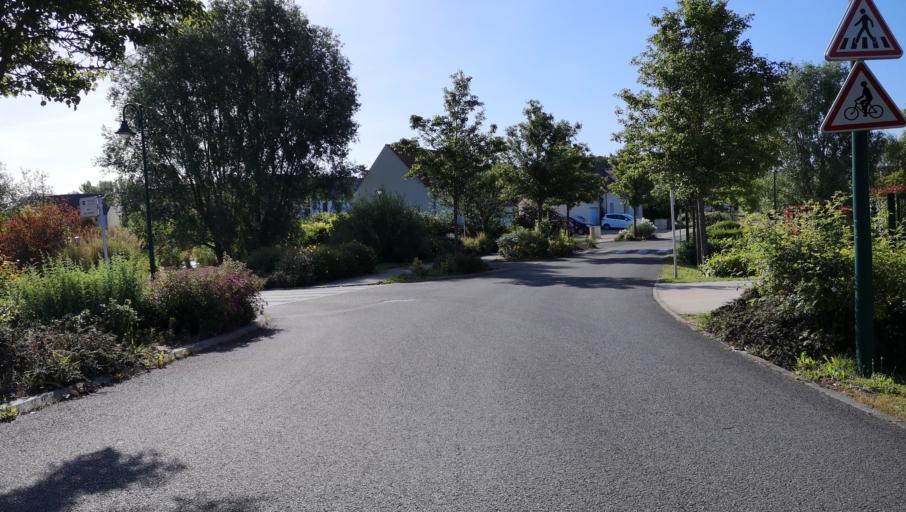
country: FR
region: Centre
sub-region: Departement du Loiret
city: Saint-Jean-de-Braye
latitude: 47.9190
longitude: 1.9734
